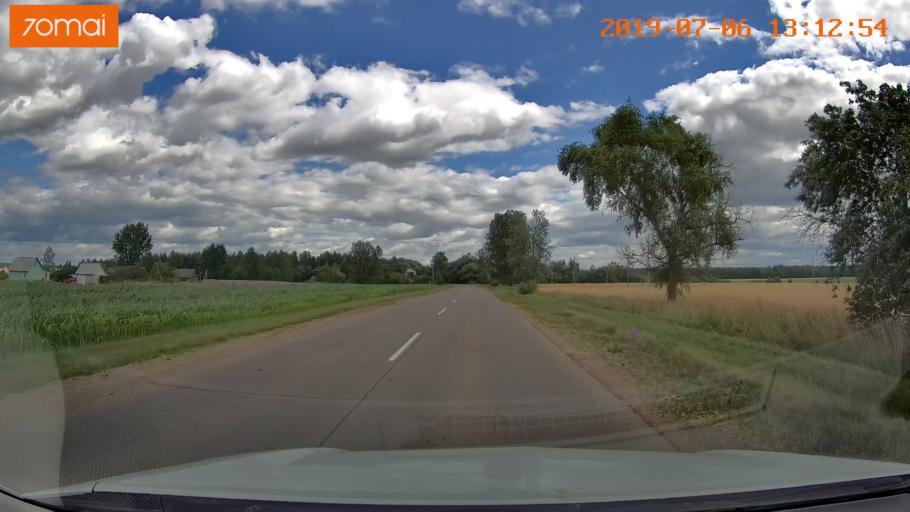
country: BY
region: Minsk
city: Enyerhyetykaw
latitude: 53.6582
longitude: 26.9977
